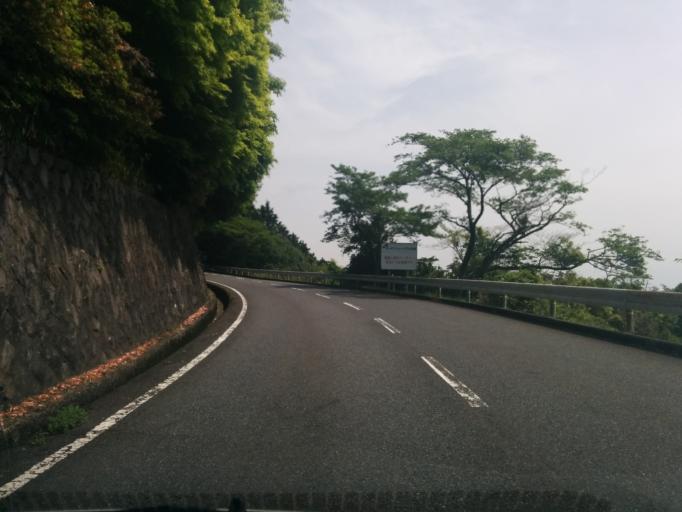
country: JP
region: Shiga Prefecture
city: Otsu-shi
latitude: 35.0343
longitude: 135.8373
